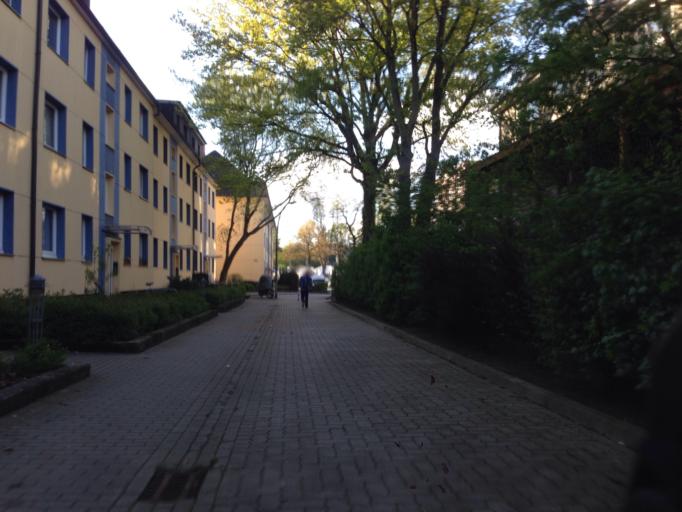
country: DE
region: Hamburg
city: Wandsbek
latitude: 53.5721
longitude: 10.0936
